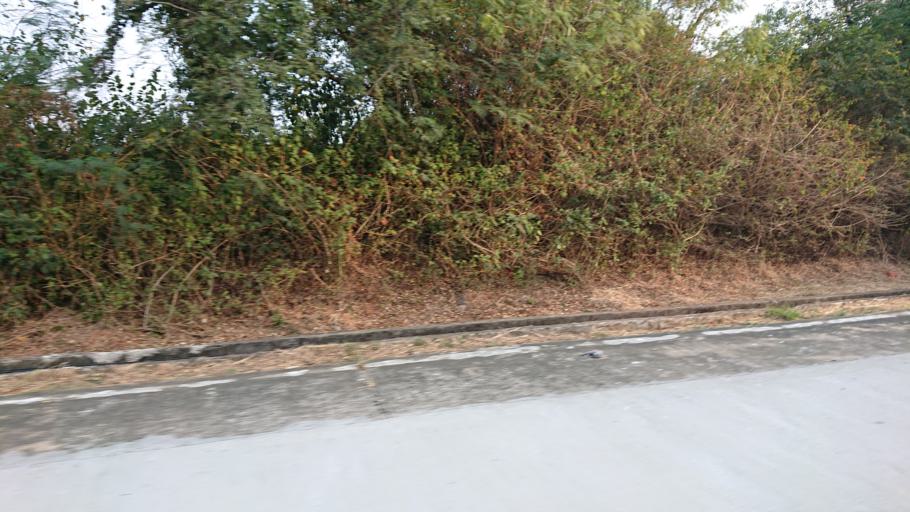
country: TW
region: Fukien
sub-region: Kinmen
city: Jincheng
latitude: 24.4442
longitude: 118.2532
